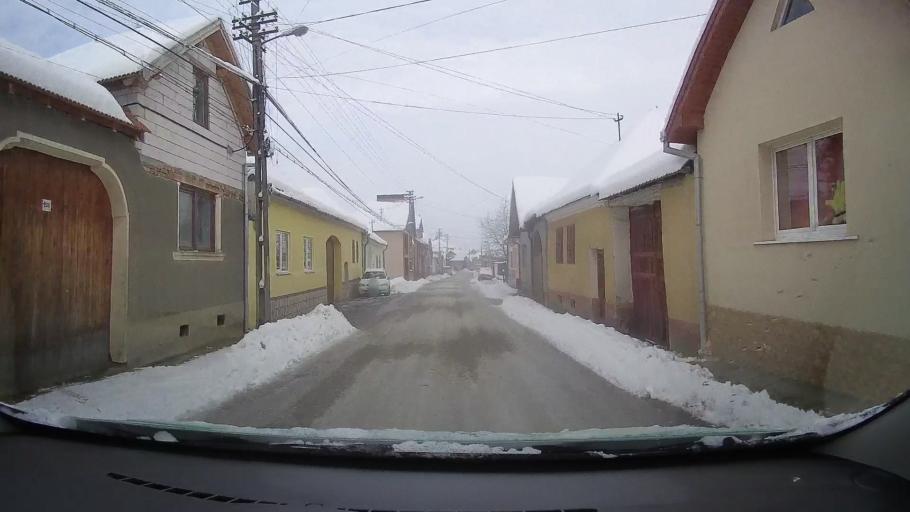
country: RO
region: Alba
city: Pianu de Sus
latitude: 45.8932
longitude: 23.4836
